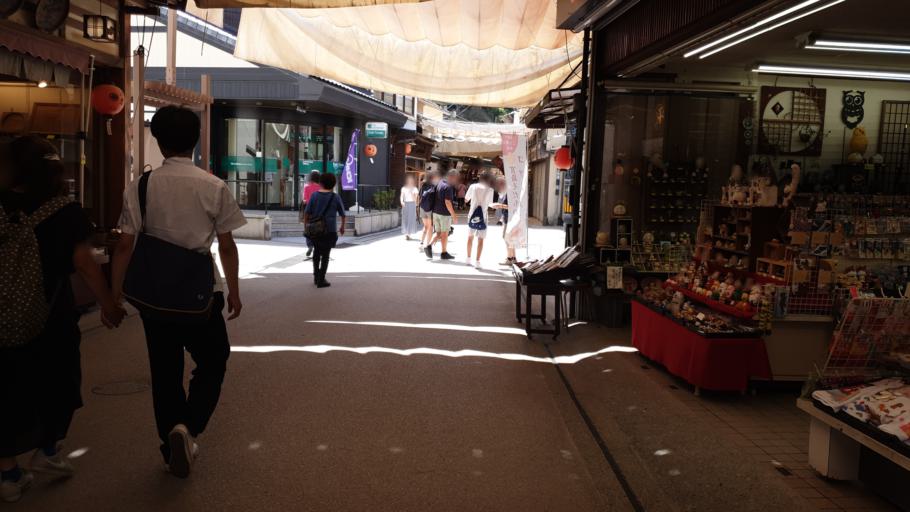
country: JP
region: Hiroshima
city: Miyajima
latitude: 34.2982
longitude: 132.3214
